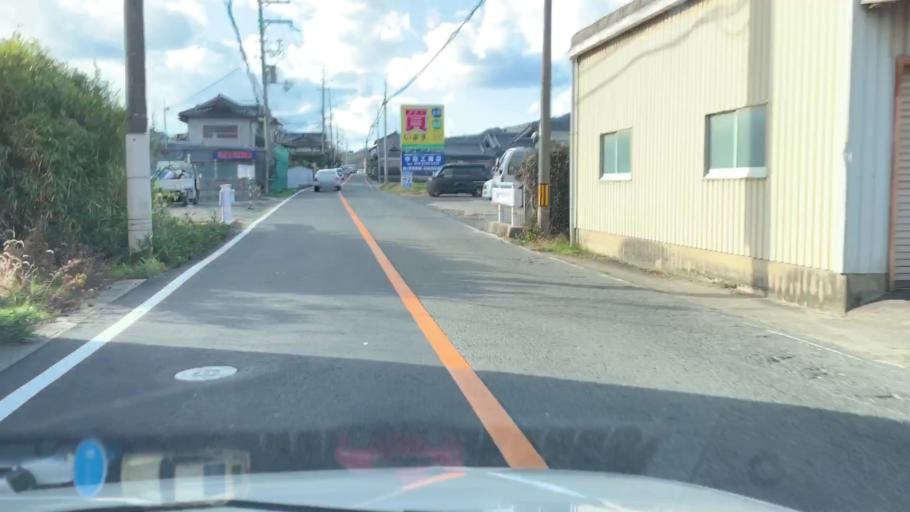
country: JP
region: Wakayama
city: Iwade
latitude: 34.2718
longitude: 135.2616
